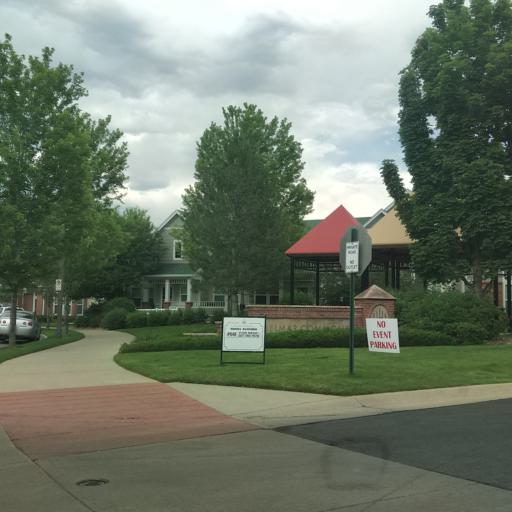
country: US
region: Colorado
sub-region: Jefferson County
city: Lakewood
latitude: 39.7055
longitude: -105.0836
